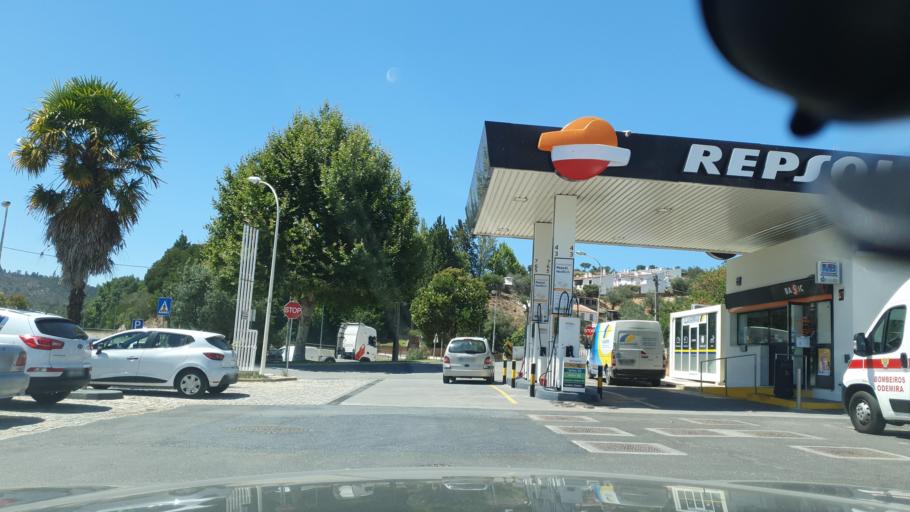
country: PT
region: Beja
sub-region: Odemira
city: Odemira
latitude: 37.5987
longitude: -8.6454
